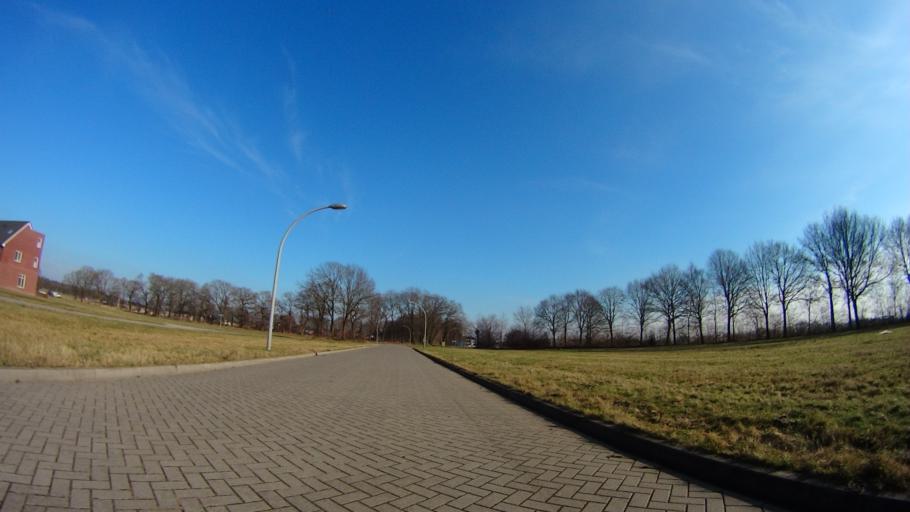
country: NL
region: Drenthe
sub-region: Gemeente Emmen
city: Emmen
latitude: 52.7547
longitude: 6.8597
